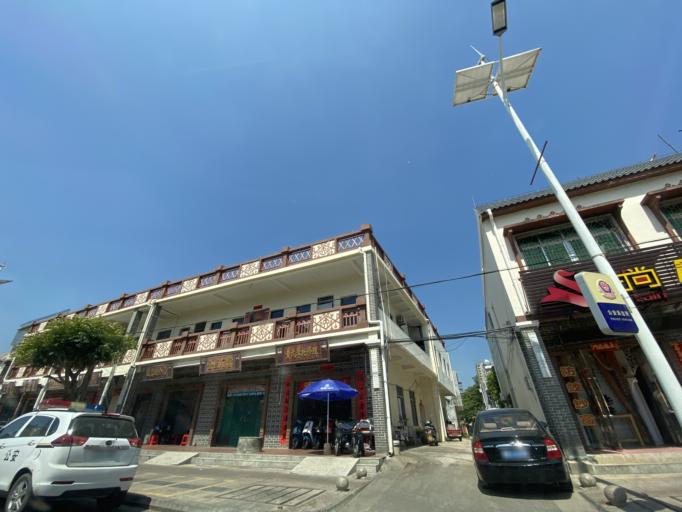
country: CN
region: Hainan
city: Yingzhou
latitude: 18.4222
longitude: 109.8489
